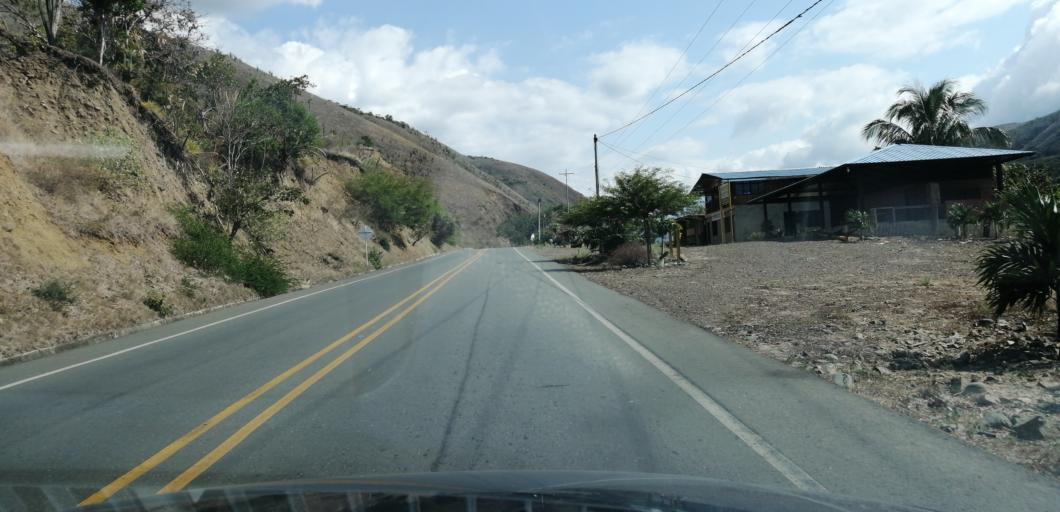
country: CO
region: Valle del Cauca
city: Dagua
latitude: 3.7393
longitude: -76.6645
